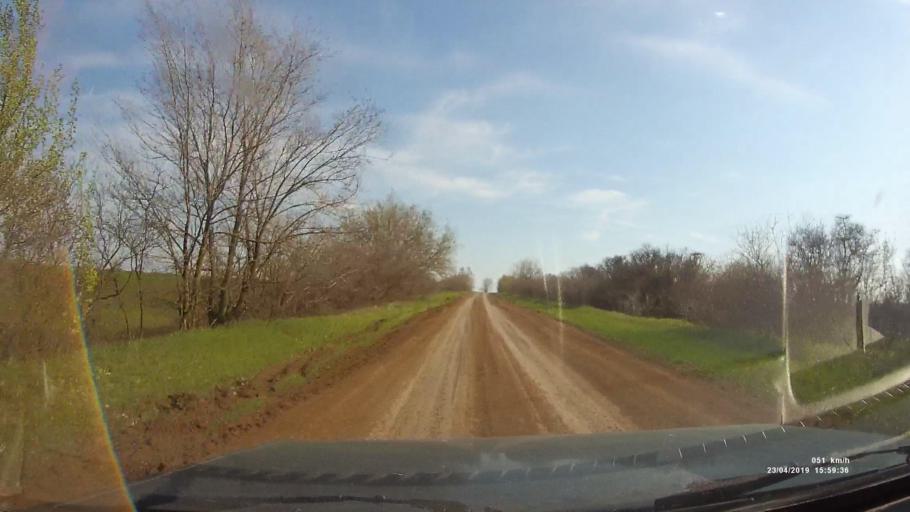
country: RU
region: Rostov
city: Remontnoye
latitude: 46.5156
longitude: 43.1096
